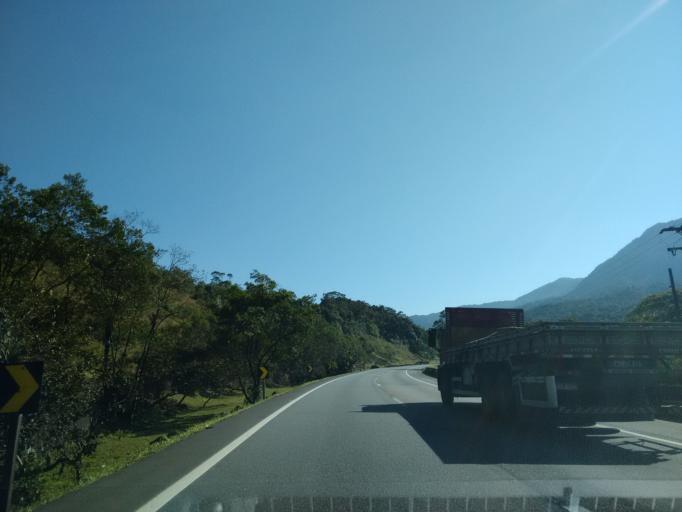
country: BR
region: Parana
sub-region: Guaratuba
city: Guaratuba
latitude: -25.9293
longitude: -48.9117
